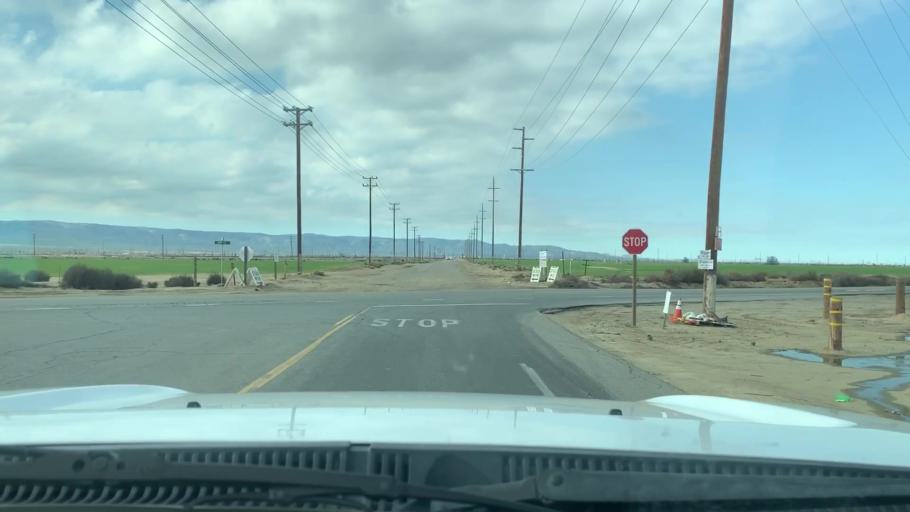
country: US
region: California
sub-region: Kern County
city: Lost Hills
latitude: 35.4991
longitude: -119.7391
